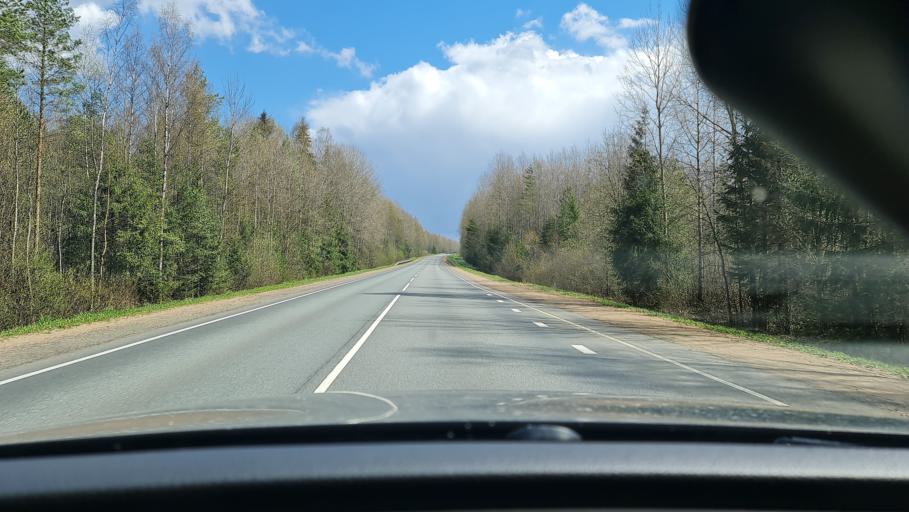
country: RU
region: Tverskaya
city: Zapadnaya Dvina
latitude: 56.3040
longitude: 32.2543
